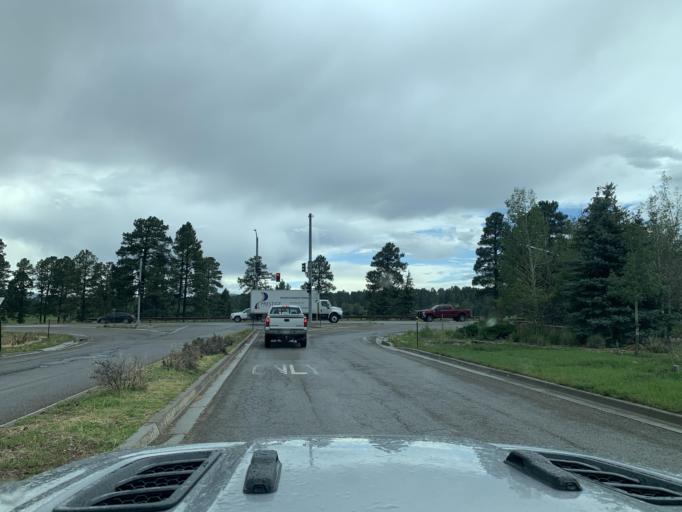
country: US
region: Colorado
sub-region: Archuleta County
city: Pagosa Springs
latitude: 37.2626
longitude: -107.0613
